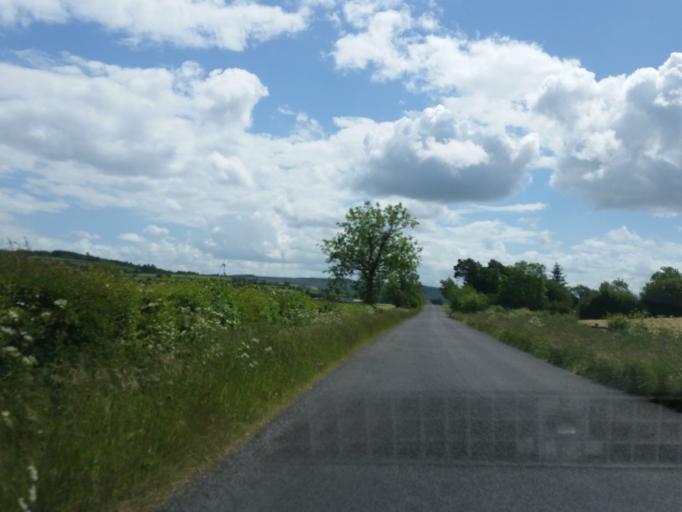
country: GB
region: Northern Ireland
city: Fivemiletown
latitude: 54.3521
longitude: -7.2981
